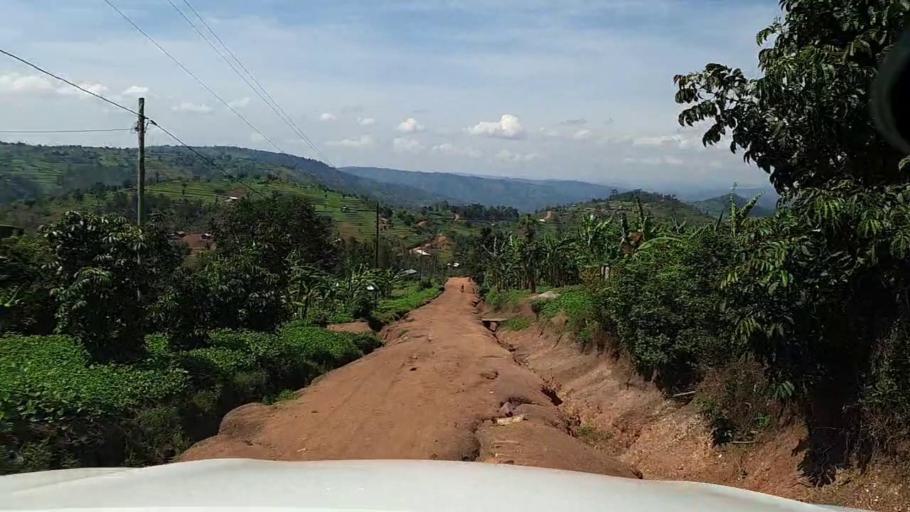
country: RW
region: Southern Province
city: Butare
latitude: -2.7224
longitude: 29.8355
